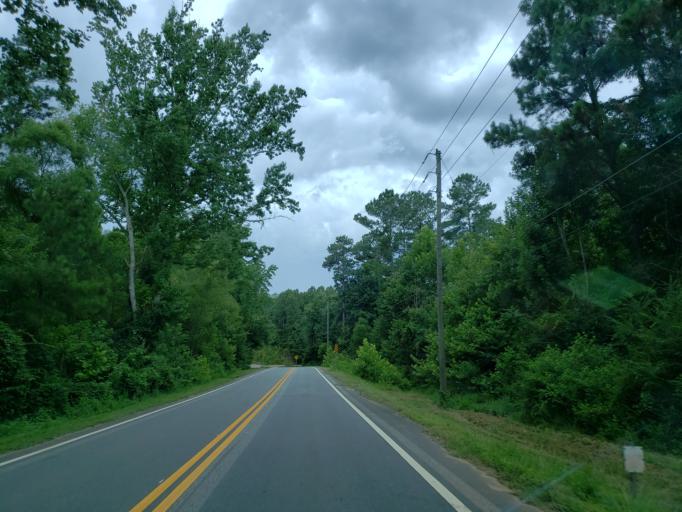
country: US
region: Georgia
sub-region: Paulding County
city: Dallas
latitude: 33.9920
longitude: -84.7902
